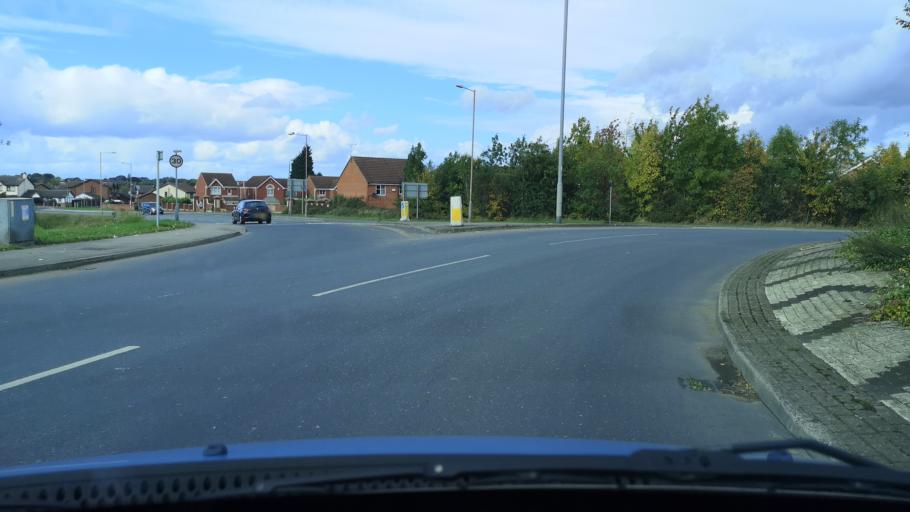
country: GB
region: England
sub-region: City and Borough of Wakefield
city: Normanton
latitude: 53.6910
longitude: -1.4021
